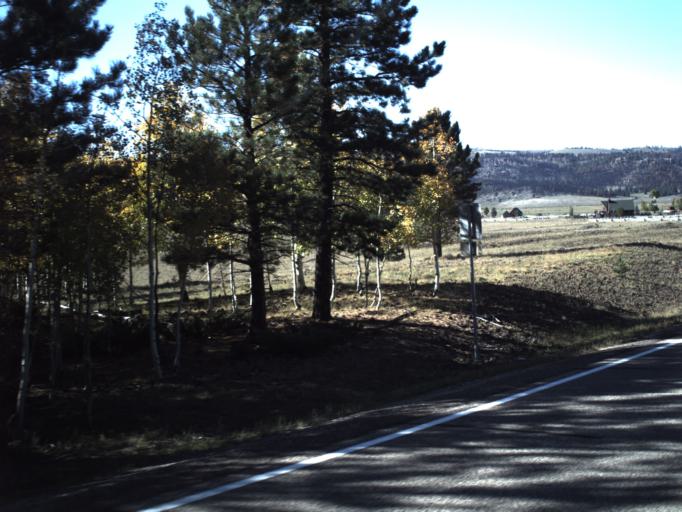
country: US
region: Utah
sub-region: Iron County
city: Parowan
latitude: 37.6736
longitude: -112.6671
